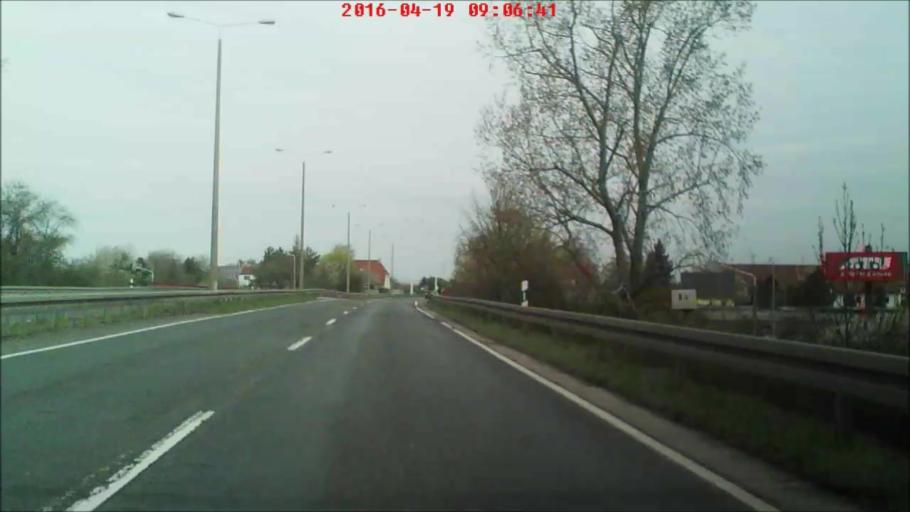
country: DE
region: Thuringia
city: Erfurt
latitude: 51.0102
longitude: 10.9883
